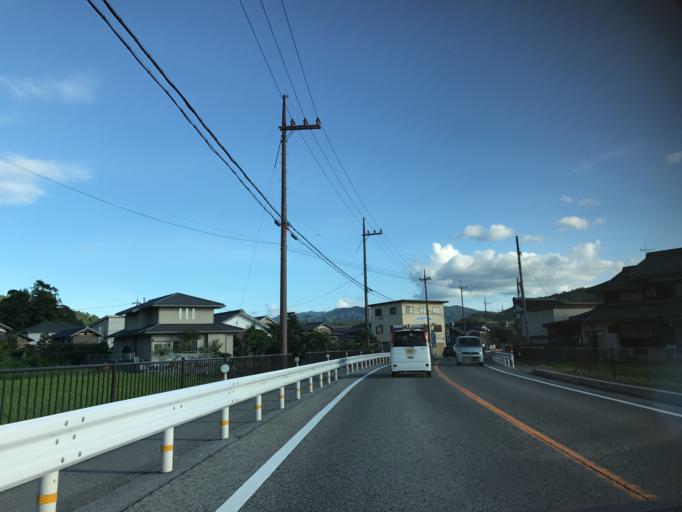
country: JP
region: Shiga Prefecture
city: Hikone
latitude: 35.2334
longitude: 136.2962
